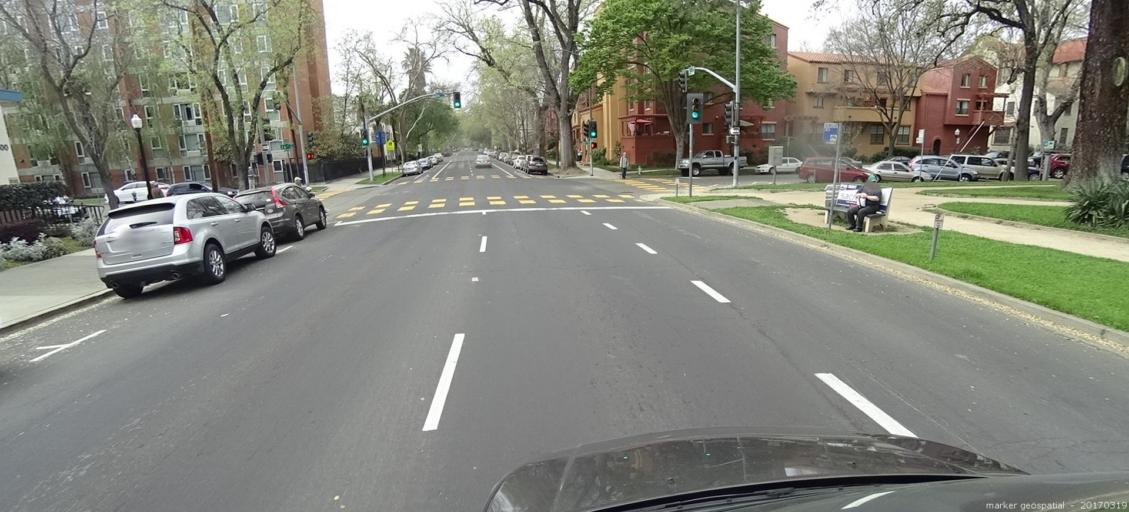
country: US
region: California
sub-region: Sacramento County
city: Sacramento
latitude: 38.5722
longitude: -121.4724
